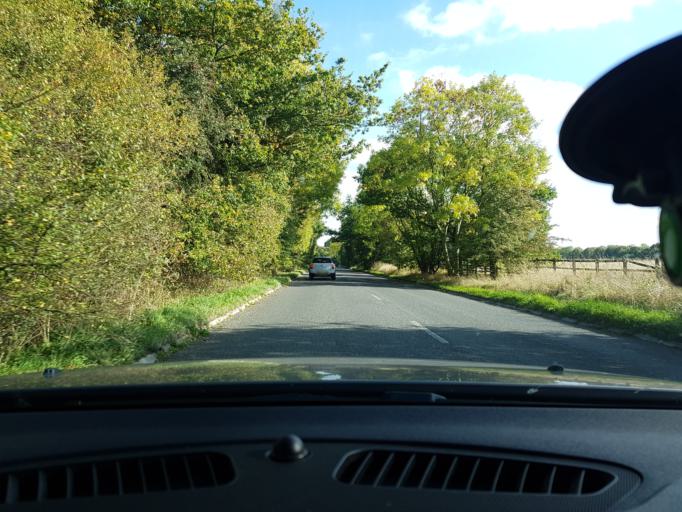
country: GB
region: England
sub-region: Wiltshire
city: Aldbourne
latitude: 51.4913
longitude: -1.5747
